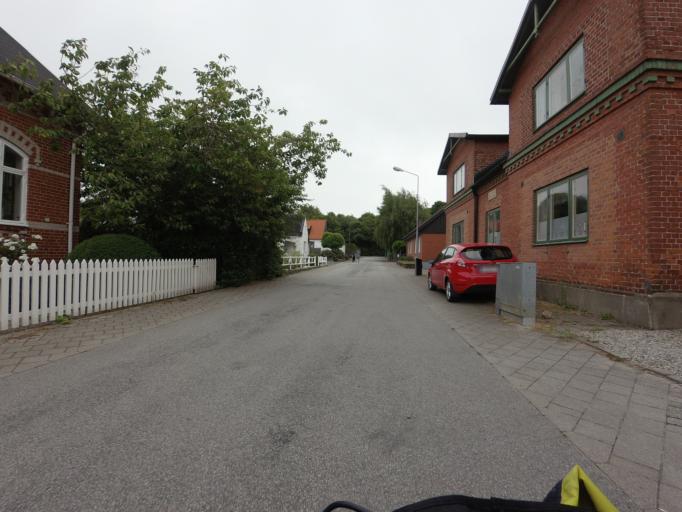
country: SE
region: Skane
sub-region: Malmo
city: Bunkeflostrand
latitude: 55.5239
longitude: 12.9301
